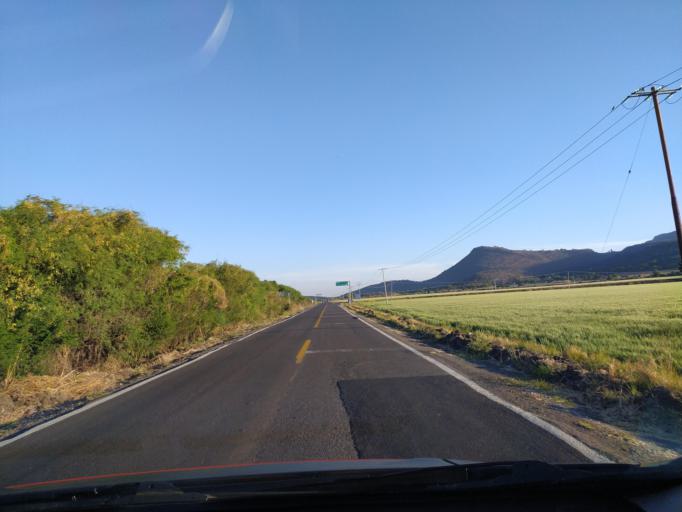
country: MX
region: Guanajuato
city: Ciudad Manuel Doblado
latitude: 20.7777
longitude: -101.8326
